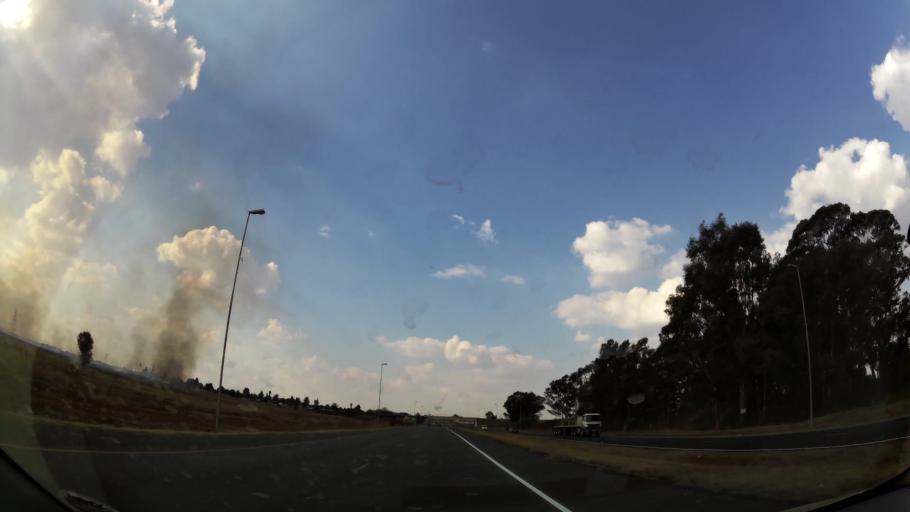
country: ZA
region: Gauteng
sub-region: Ekurhuleni Metropolitan Municipality
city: Boksburg
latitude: -26.2704
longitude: 28.2858
